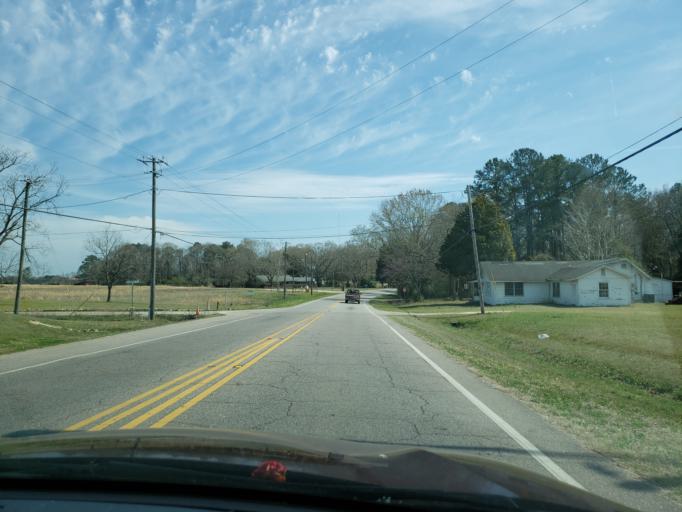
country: US
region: Alabama
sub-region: Elmore County
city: Tallassee
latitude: 32.5647
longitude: -85.9316
